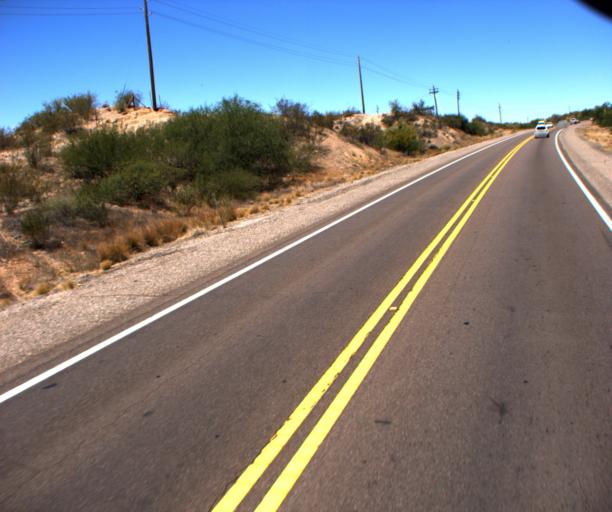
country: US
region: Arizona
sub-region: Maricopa County
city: Wickenburg
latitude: 33.9921
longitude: -112.7502
